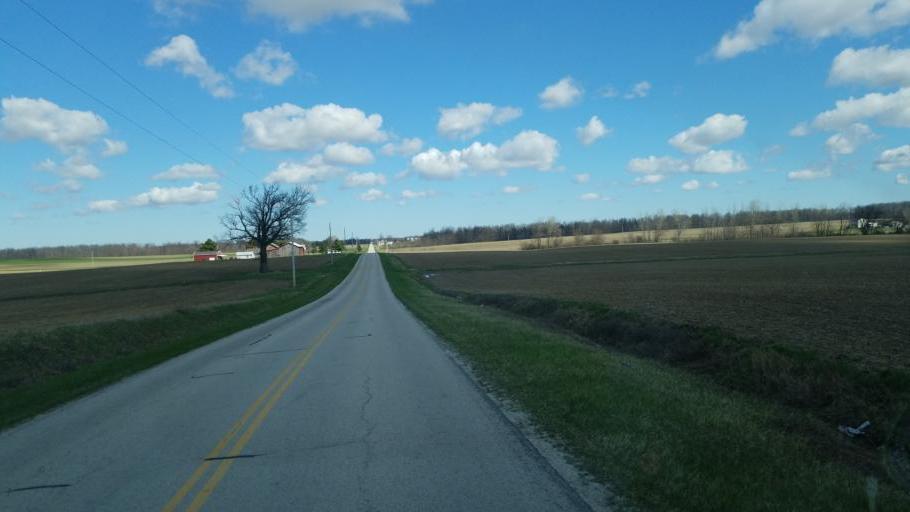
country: US
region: Ohio
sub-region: Sandusky County
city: Mount Carmel
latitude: 41.1426
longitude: -82.9382
